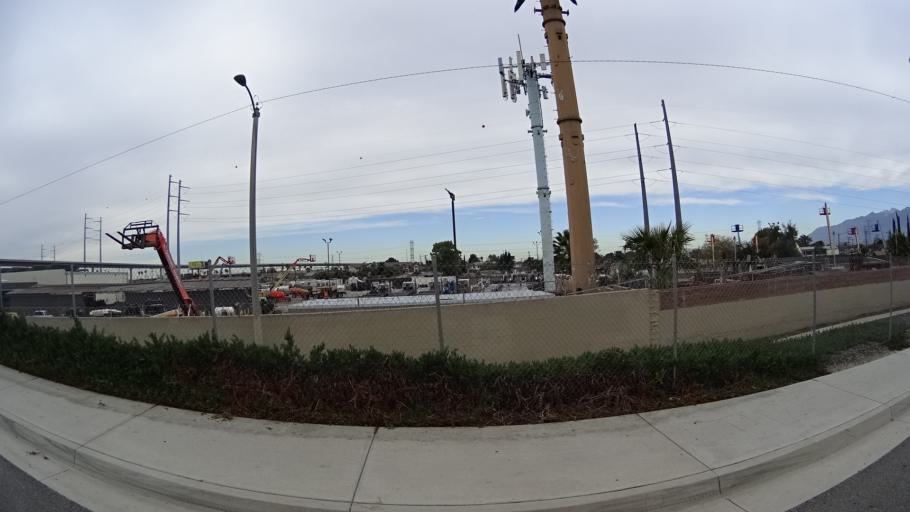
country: US
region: California
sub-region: Los Angeles County
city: West Puente Valley
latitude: 34.0674
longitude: -117.9939
